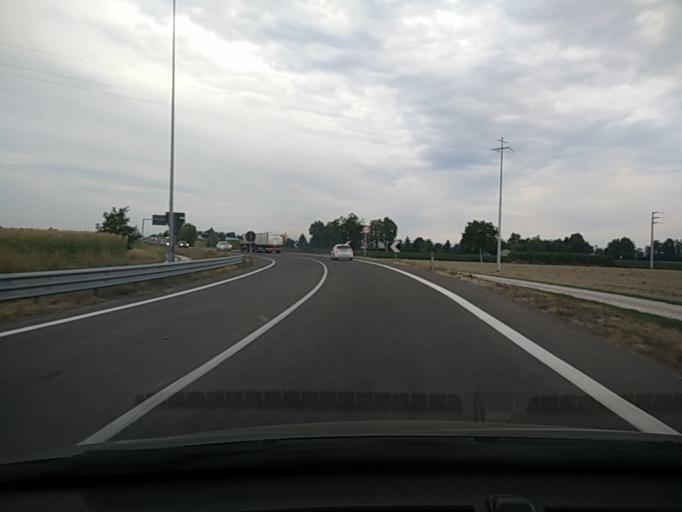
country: IT
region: Veneto
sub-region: Provincia di Venezia
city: Musile di Piave
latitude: 45.5821
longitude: 12.5586
